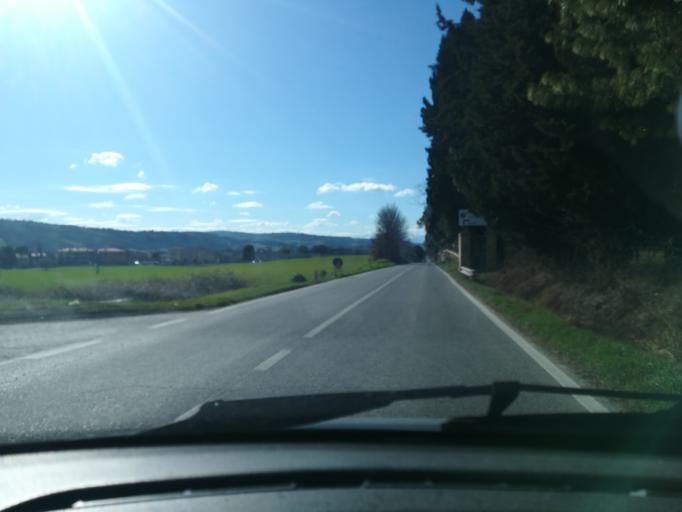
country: IT
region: The Marches
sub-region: Provincia di Macerata
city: Montecassiano
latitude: 43.3505
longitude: 13.4361
